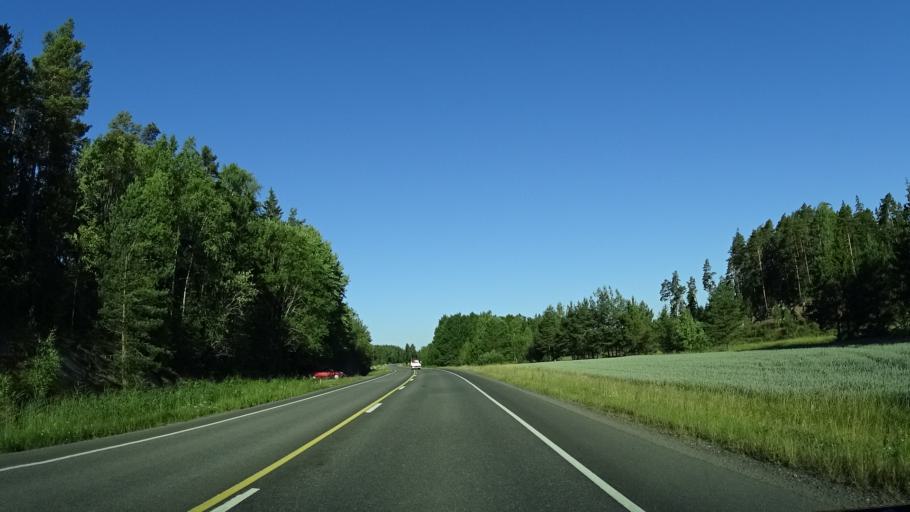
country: FI
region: Varsinais-Suomi
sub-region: Turku
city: Naantali
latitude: 60.4603
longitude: 21.9754
